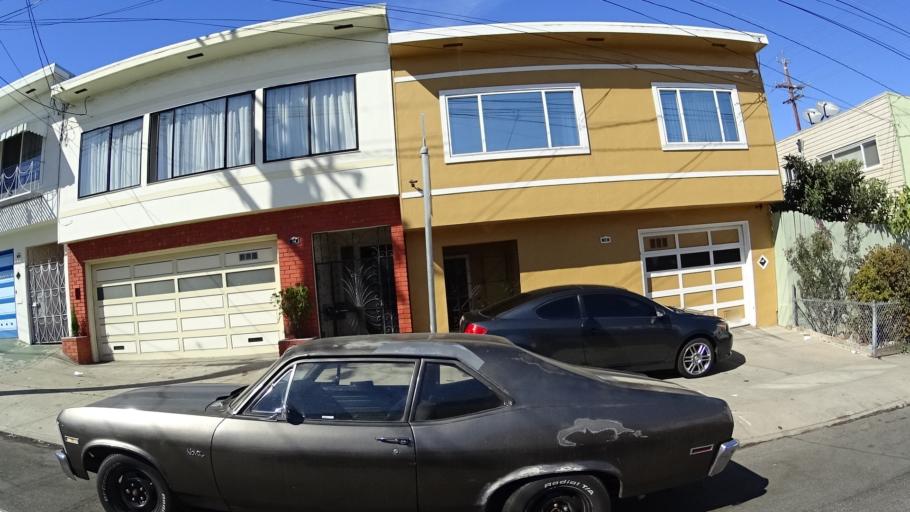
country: US
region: California
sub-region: San Mateo County
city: Brisbane
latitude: 37.7228
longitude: -122.3985
